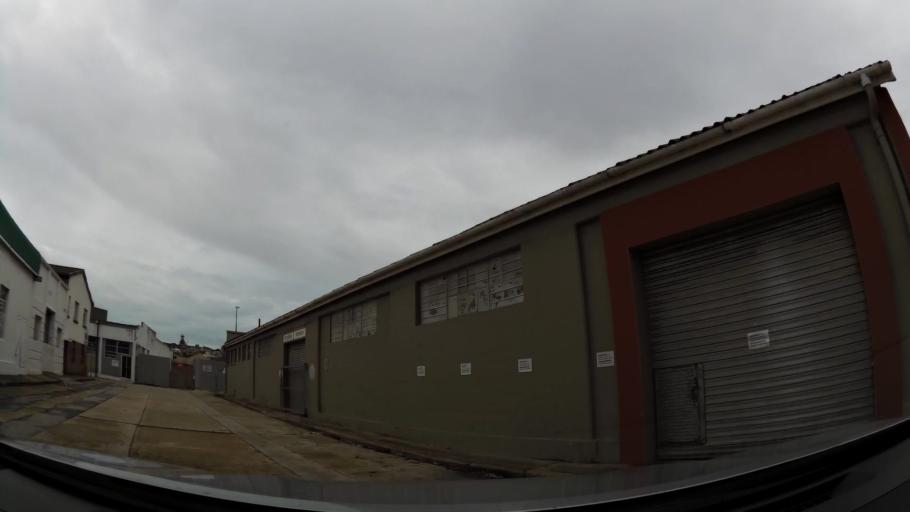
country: ZA
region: Eastern Cape
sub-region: Nelson Mandela Bay Metropolitan Municipality
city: Port Elizabeth
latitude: -33.9509
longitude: 25.6104
